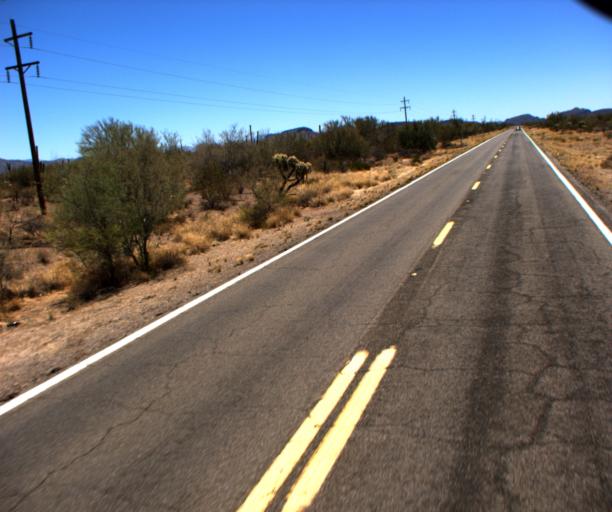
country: US
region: Arizona
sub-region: Pima County
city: Sells
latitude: 32.0212
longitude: -112.0023
